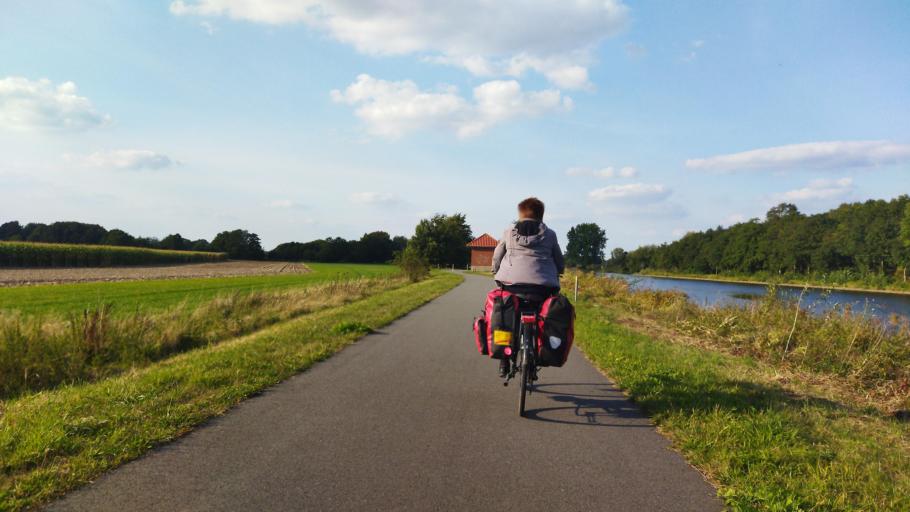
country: DE
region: Lower Saxony
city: Lehe
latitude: 53.0206
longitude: 7.3213
